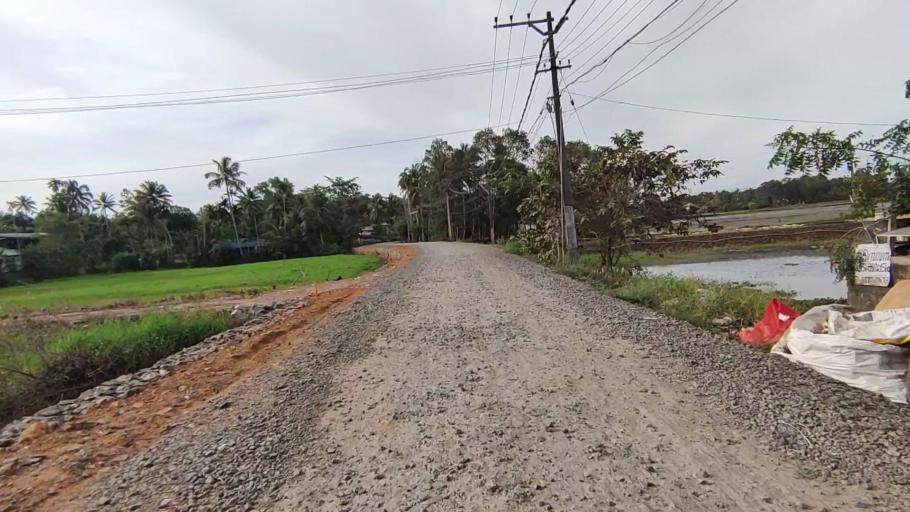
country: IN
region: Kerala
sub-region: Kottayam
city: Kottayam
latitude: 9.5781
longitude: 76.4920
